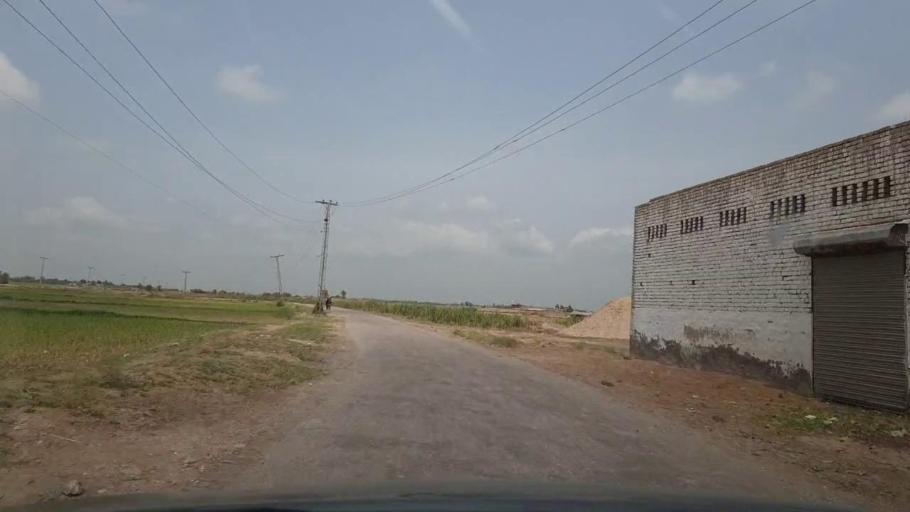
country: PK
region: Sindh
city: Ratodero
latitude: 27.9026
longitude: 68.3197
